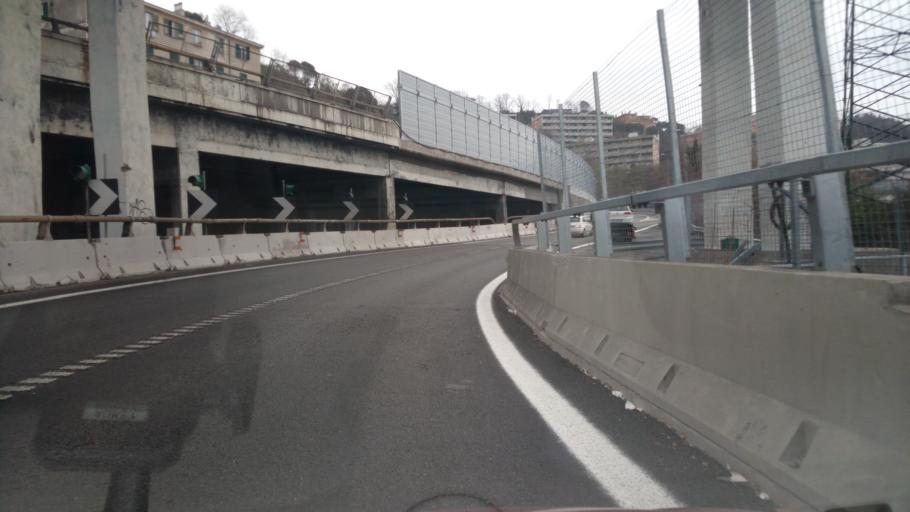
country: IT
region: Liguria
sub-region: Provincia di Genova
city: San Teodoro
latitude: 44.4237
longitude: 8.8935
